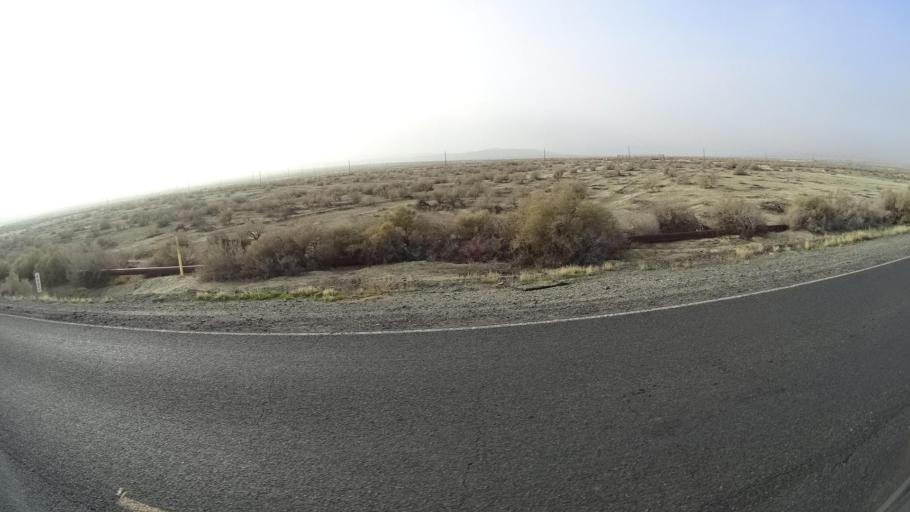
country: US
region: California
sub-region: Kern County
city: Ford City
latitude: 35.2196
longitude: -119.4456
